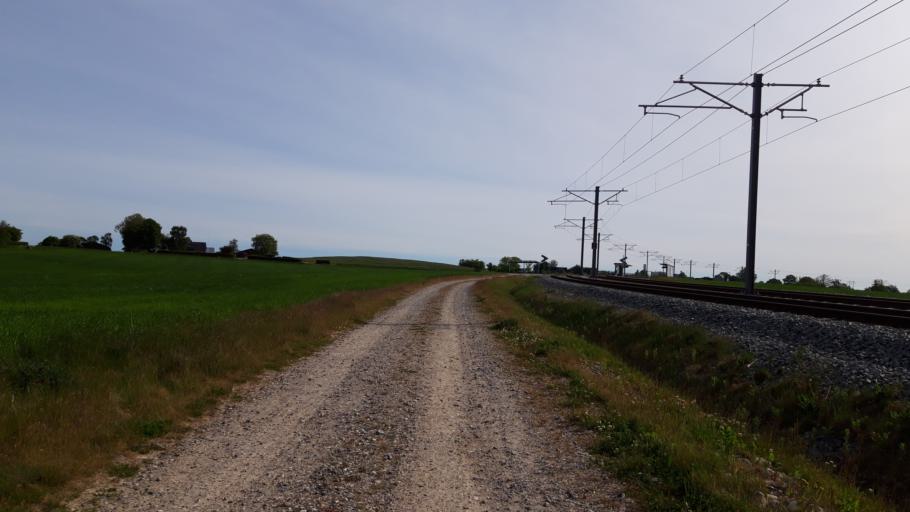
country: DK
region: Central Jutland
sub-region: Arhus Kommune
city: Lystrup
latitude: 56.2263
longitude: 10.1984
